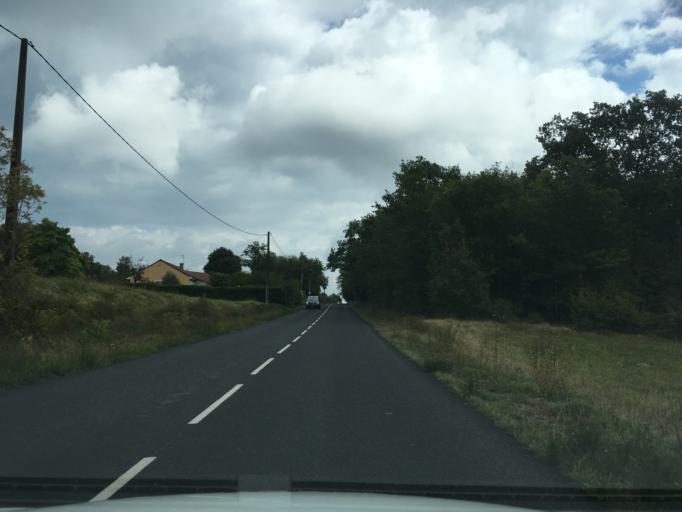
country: FR
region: Limousin
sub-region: Departement de la Correze
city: Brive-la-Gaillarde
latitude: 45.1055
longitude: 1.5443
